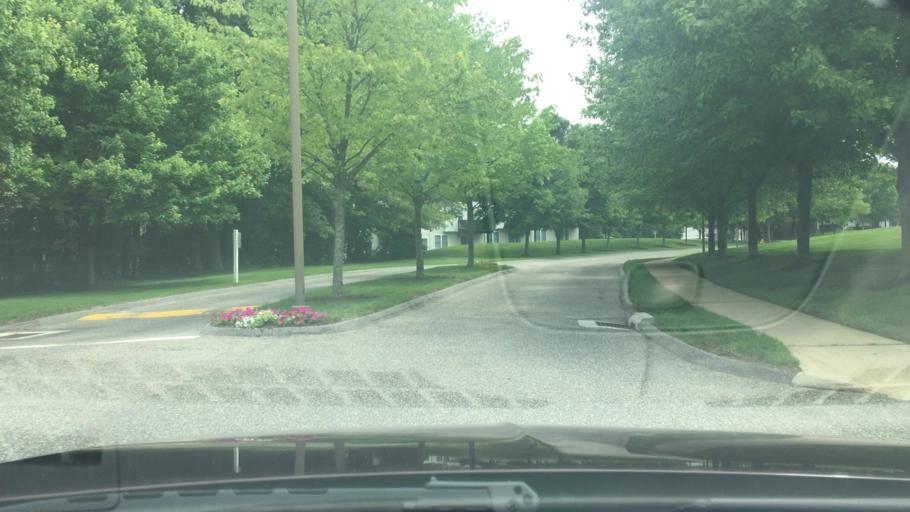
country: US
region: Connecticut
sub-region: Fairfield County
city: Danbury
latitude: 41.4327
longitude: -73.4208
